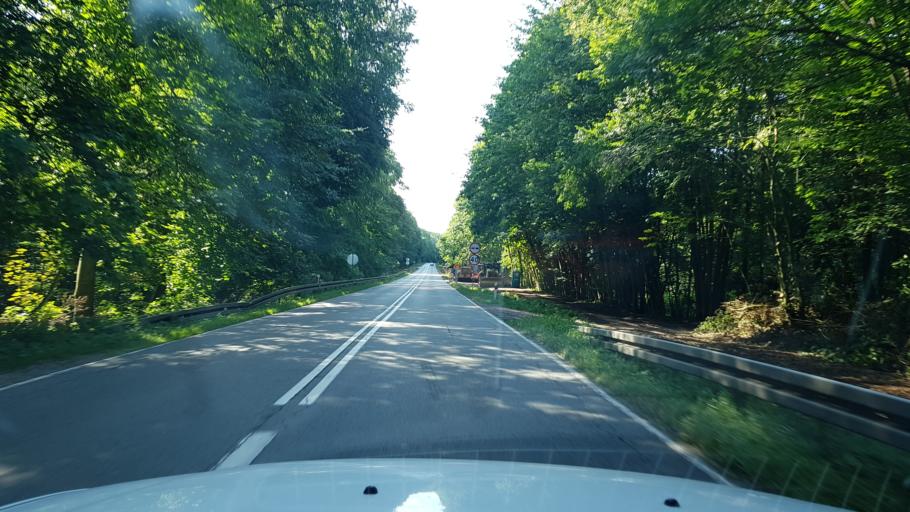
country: PL
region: West Pomeranian Voivodeship
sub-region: Powiat gryfinski
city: Stare Czarnowo
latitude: 53.3326
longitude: 14.7753
